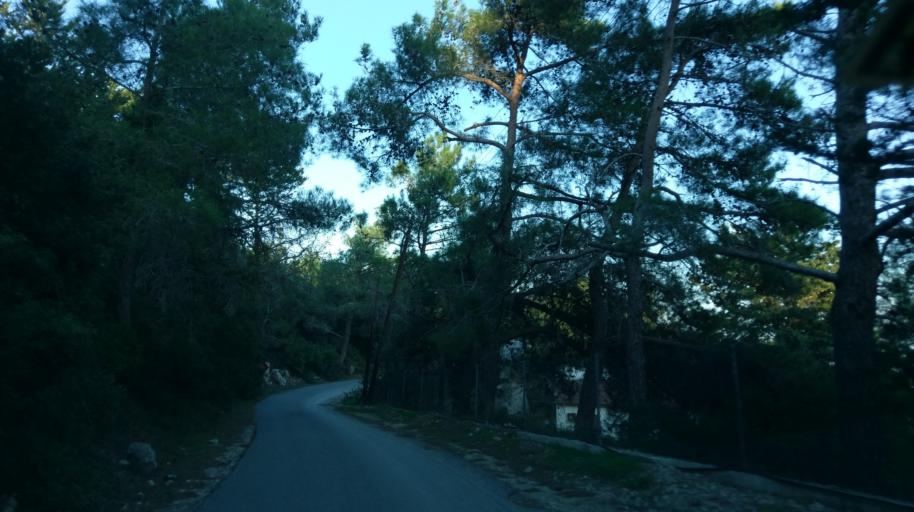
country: CY
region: Ammochostos
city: Trikomo
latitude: 35.3884
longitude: 33.8999
